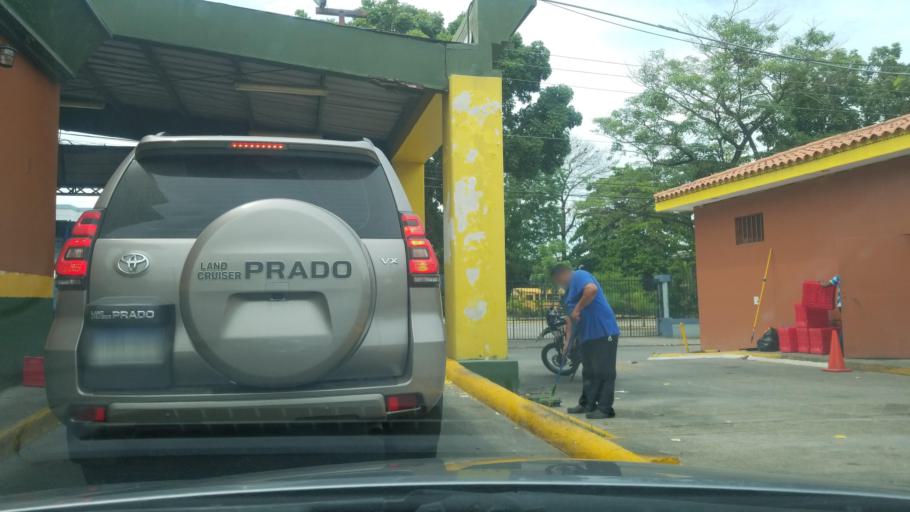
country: HN
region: Cortes
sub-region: San Pedro Sula
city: Pena Blanca
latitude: 15.5385
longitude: -88.0156
